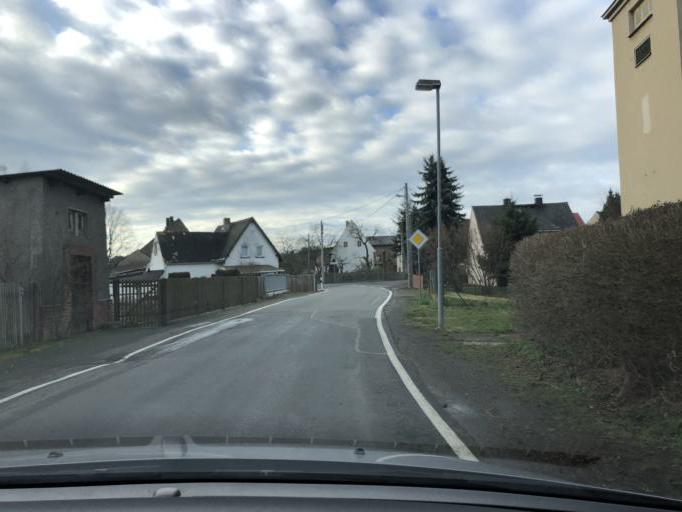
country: DE
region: Saxony
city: Grossbothen
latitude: 51.2103
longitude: 12.7877
